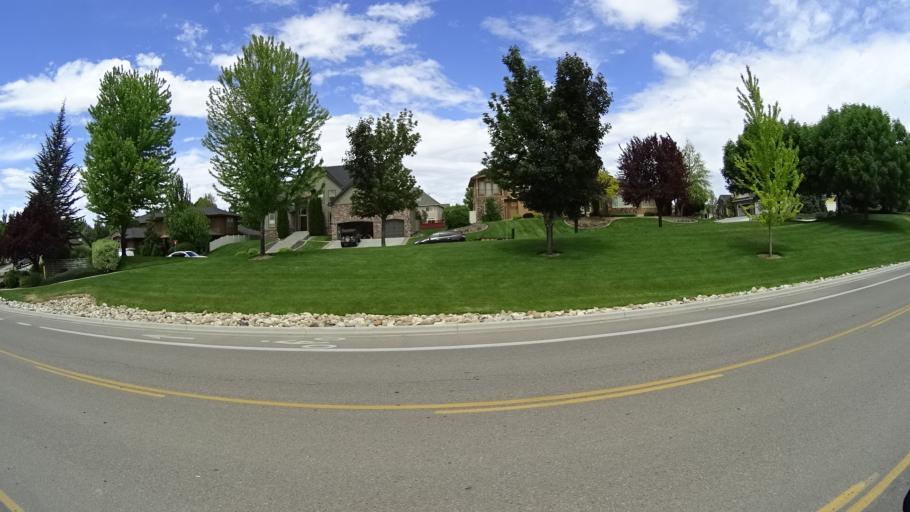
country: US
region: Idaho
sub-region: Ada County
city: Meridian
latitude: 43.5756
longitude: -116.3860
